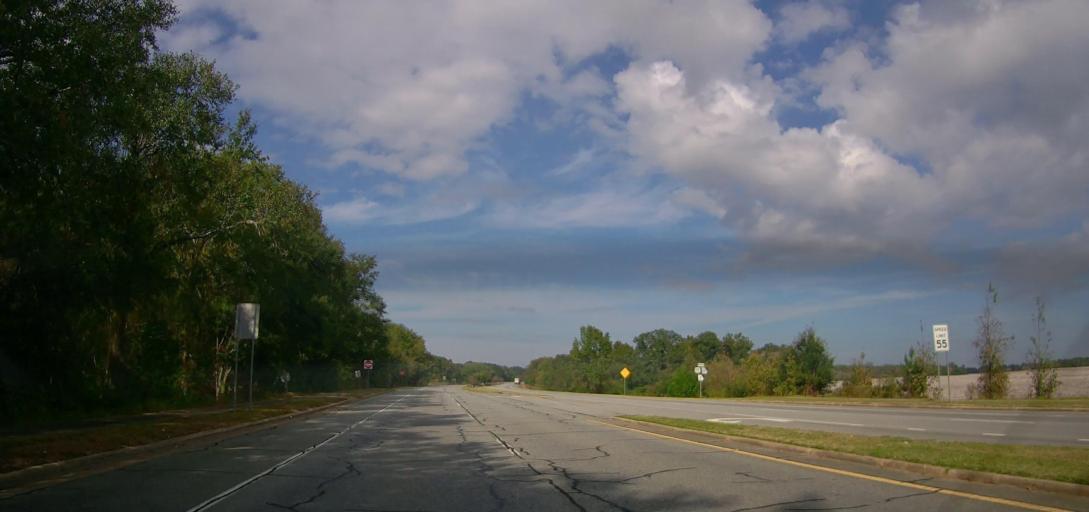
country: US
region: Georgia
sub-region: Mitchell County
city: Camilla
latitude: 31.2417
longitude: -84.2001
